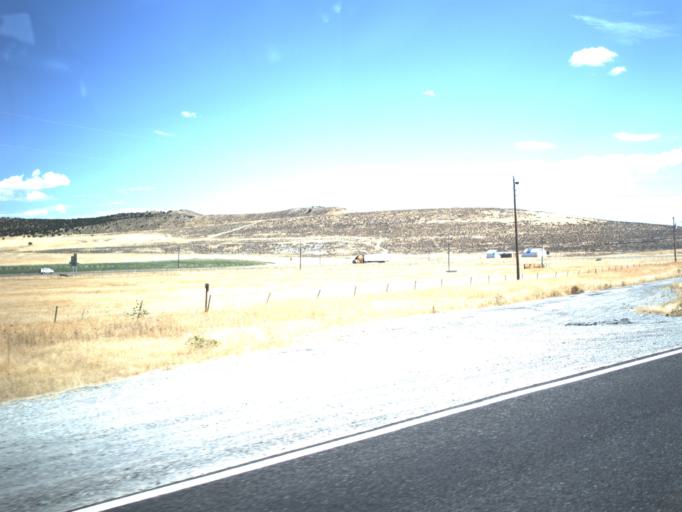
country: US
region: Idaho
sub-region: Oneida County
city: Malad City
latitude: 41.9661
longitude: -112.7693
